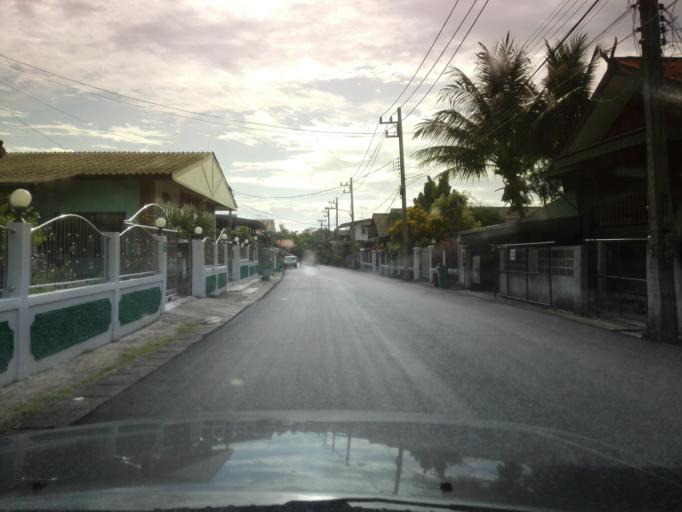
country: TH
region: Tak
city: Mae Ramat
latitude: 16.9819
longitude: 98.5168
